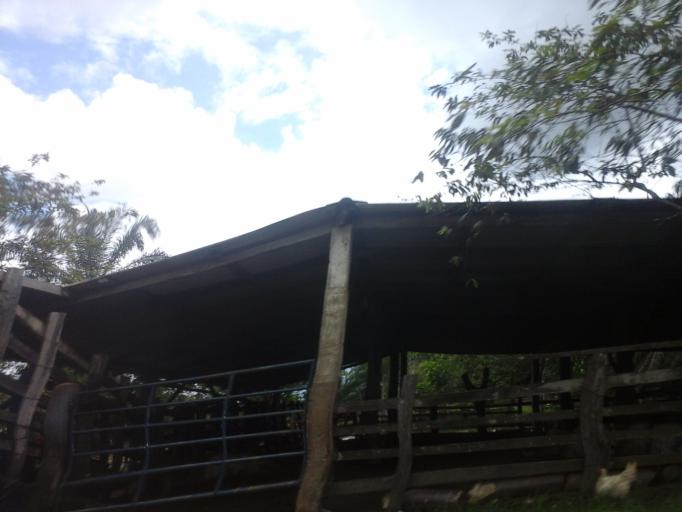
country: CO
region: Caqueta
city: El Doncello
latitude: 1.6427
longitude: -75.1667
